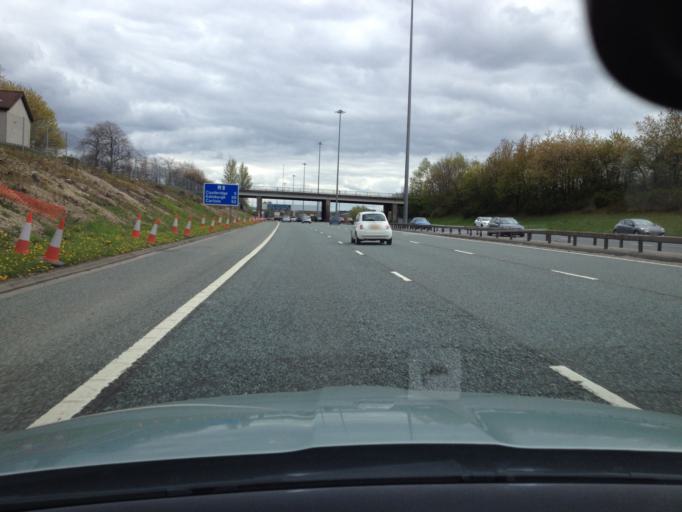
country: GB
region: Scotland
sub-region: North Lanarkshire
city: Stepps
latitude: 55.8642
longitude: -4.1244
